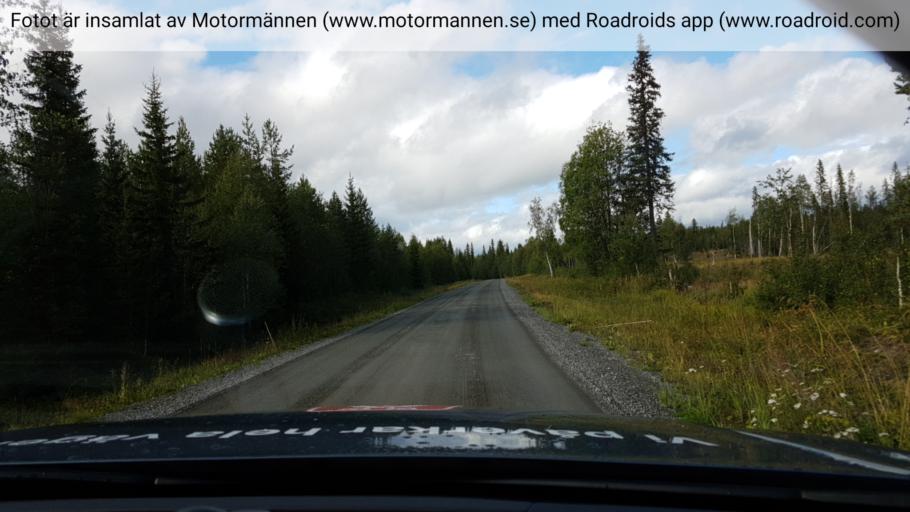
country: SE
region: Jaemtland
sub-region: Krokoms Kommun
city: Krokom
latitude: 63.7258
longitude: 14.5110
